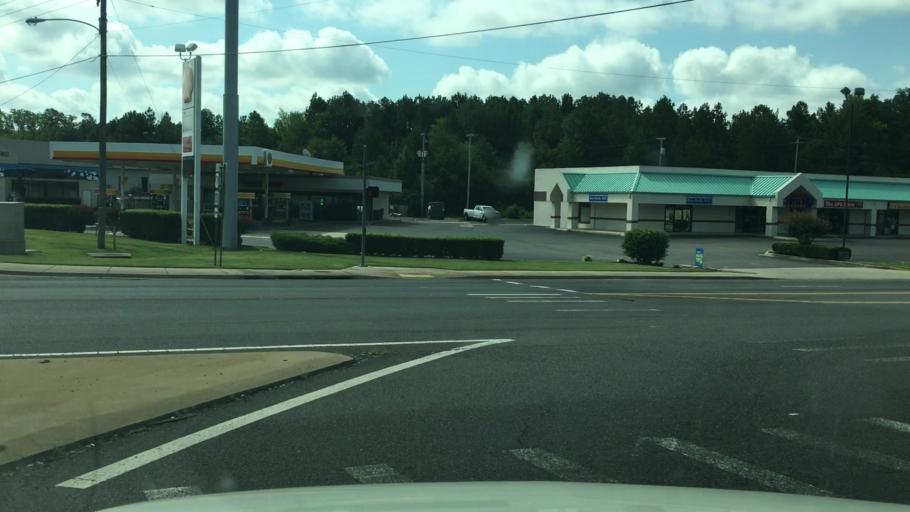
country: US
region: Arkansas
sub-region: Garland County
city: Hot Springs
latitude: 34.4648
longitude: -93.0734
